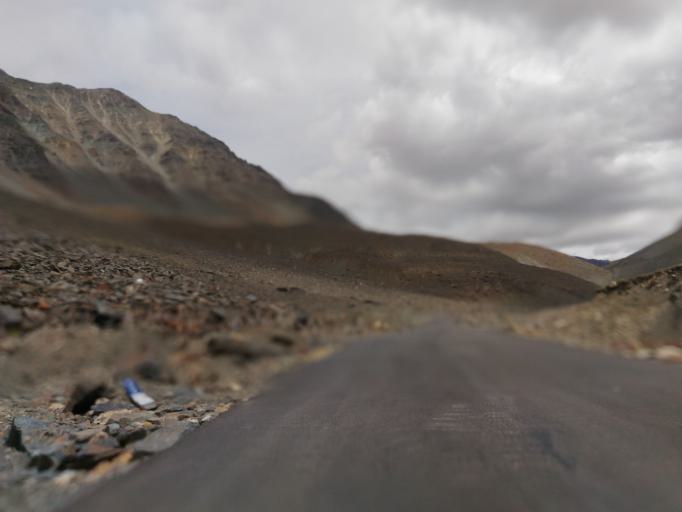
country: IN
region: Himachal Pradesh
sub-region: Lahul and Spiti
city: Kyelang
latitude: 32.7664
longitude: 77.3871
